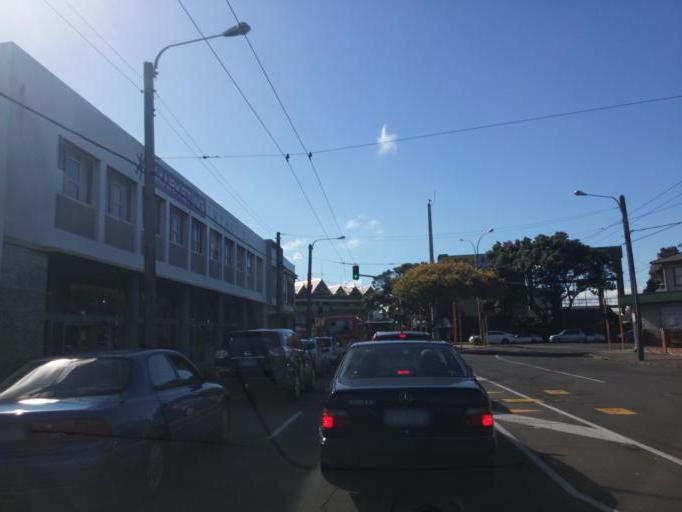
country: NZ
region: Wellington
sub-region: Wellington City
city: Wellington
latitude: -41.3017
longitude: 174.7796
